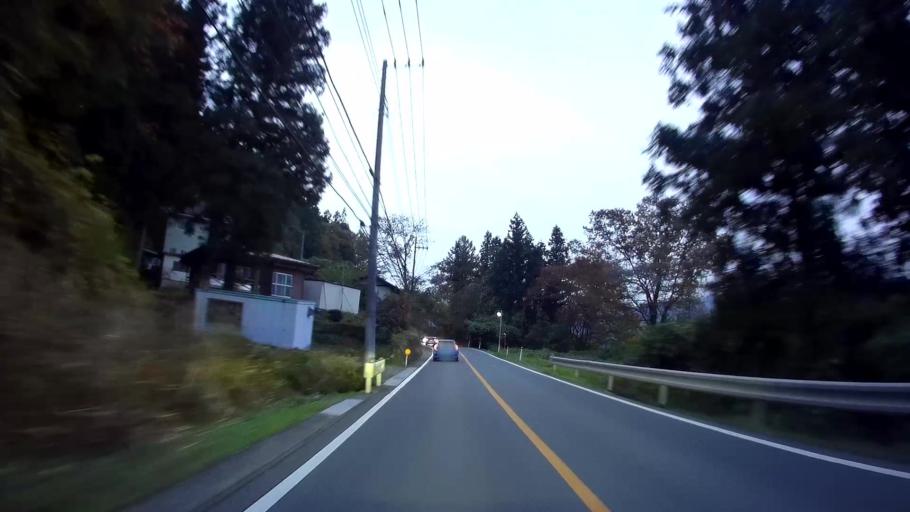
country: JP
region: Gunma
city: Nakanojomachi
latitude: 36.5413
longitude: 138.7925
